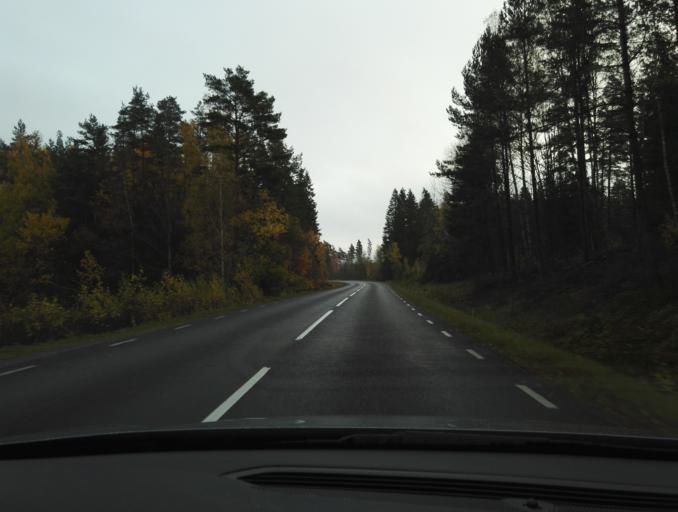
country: SE
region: Kronoberg
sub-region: Vaxjo Kommun
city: Vaexjoe
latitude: 57.0068
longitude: 14.7593
